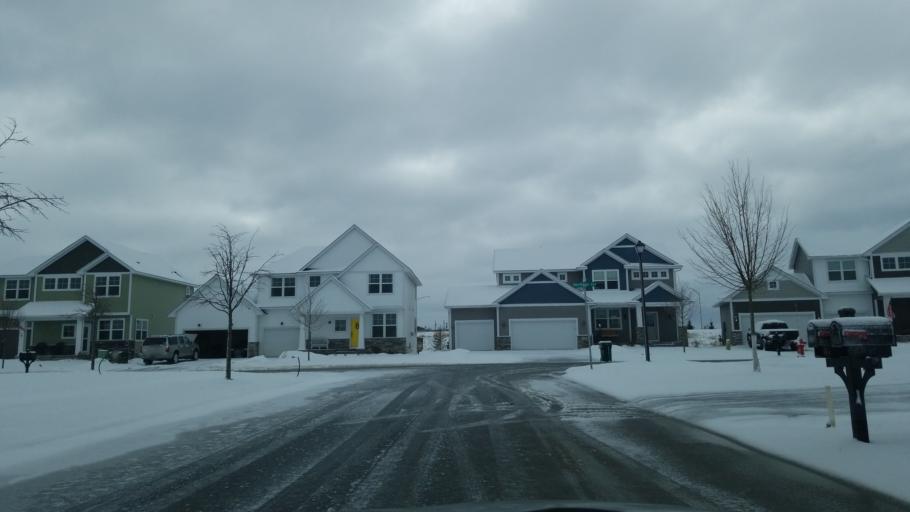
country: US
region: Wisconsin
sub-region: Saint Croix County
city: Hudson
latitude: 44.9503
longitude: -92.6982
